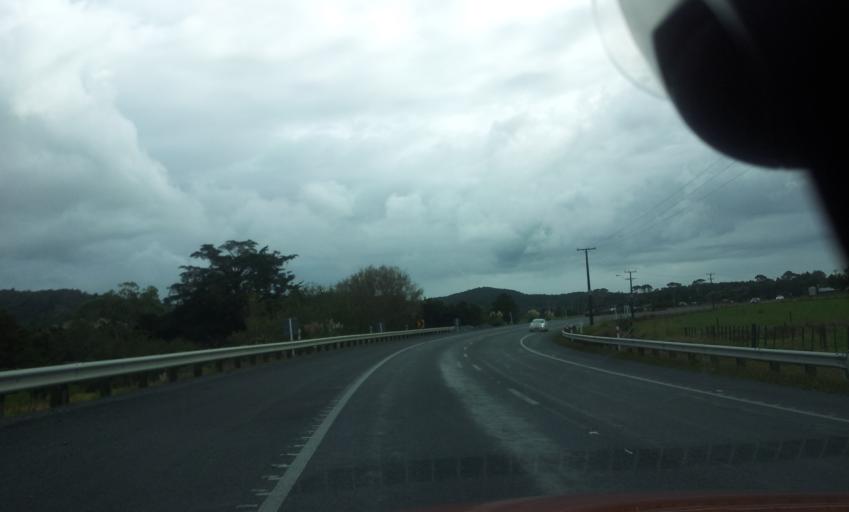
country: NZ
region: Northland
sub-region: Whangarei
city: Ruakaka
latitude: -36.0041
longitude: 174.4147
